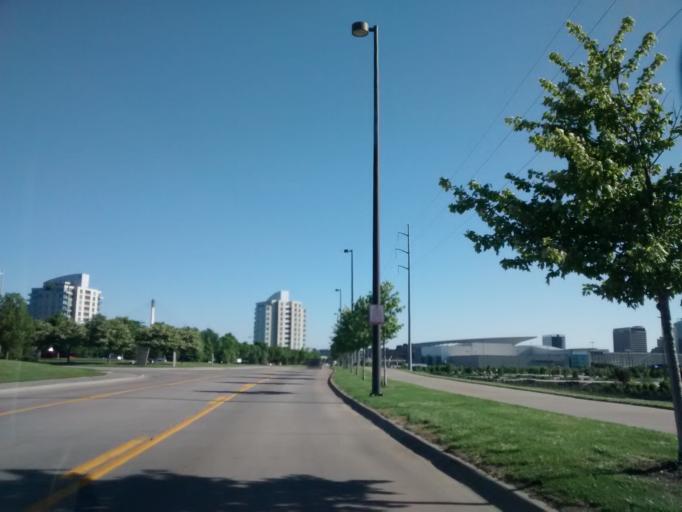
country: US
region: Nebraska
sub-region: Douglas County
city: Omaha
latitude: 41.2709
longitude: -95.9251
